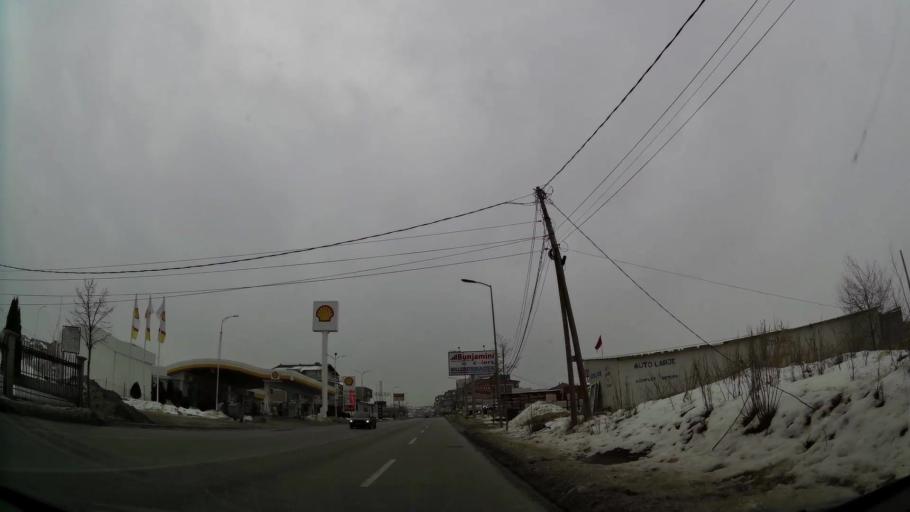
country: XK
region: Pristina
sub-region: Komuna e Prishtines
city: Pristina
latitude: 42.6983
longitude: 21.1595
